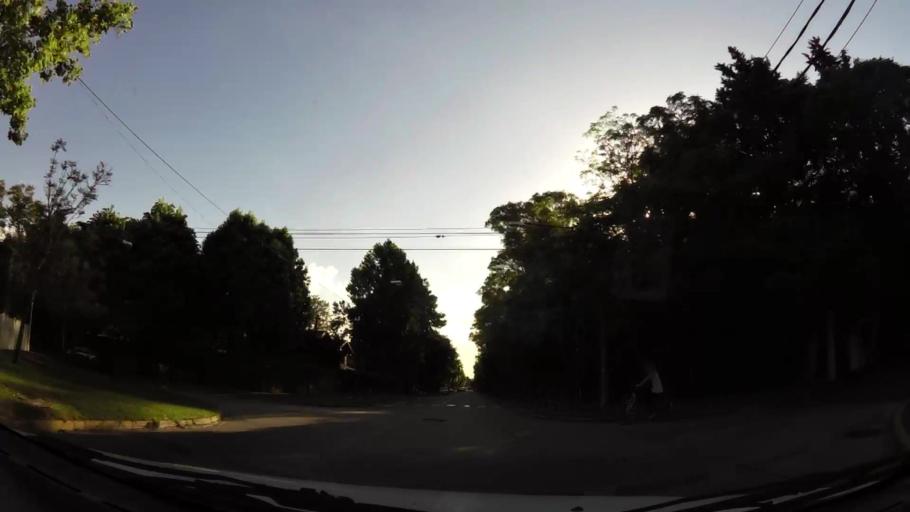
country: AR
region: Buenos Aires
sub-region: Partido de San Isidro
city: San Isidro
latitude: -34.4836
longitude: -58.5416
